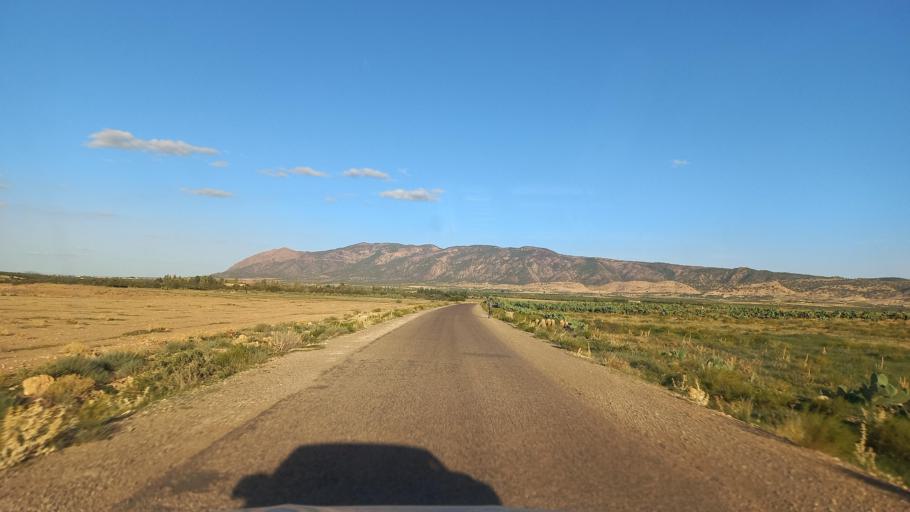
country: TN
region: Al Qasrayn
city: Sbiba
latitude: 35.4111
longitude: 9.1407
